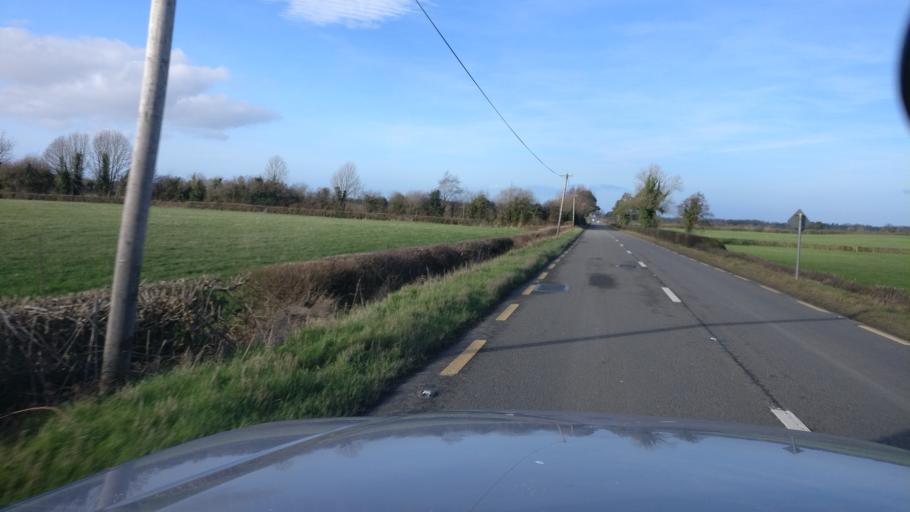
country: IE
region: Leinster
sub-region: Laois
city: Mountmellick
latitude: 53.0868
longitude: -7.3337
